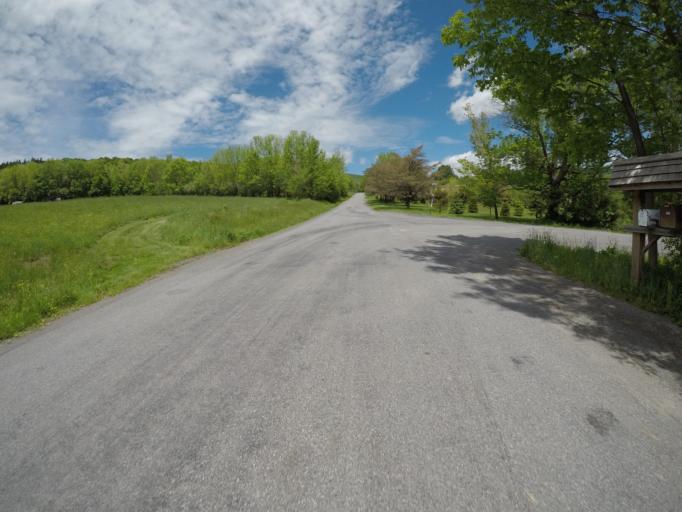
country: US
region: New York
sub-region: Delaware County
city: Stamford
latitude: 42.2694
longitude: -74.5189
